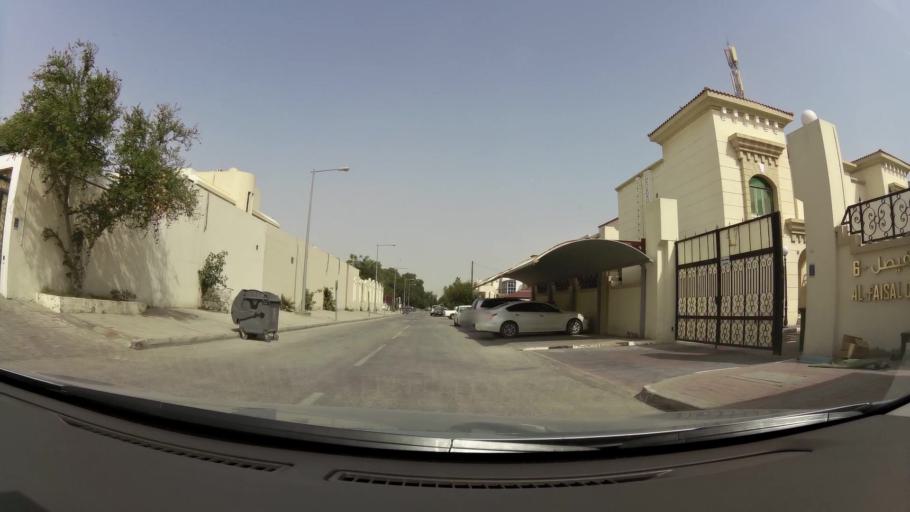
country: QA
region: Baladiyat ad Dawhah
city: Doha
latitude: 25.2773
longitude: 51.4892
